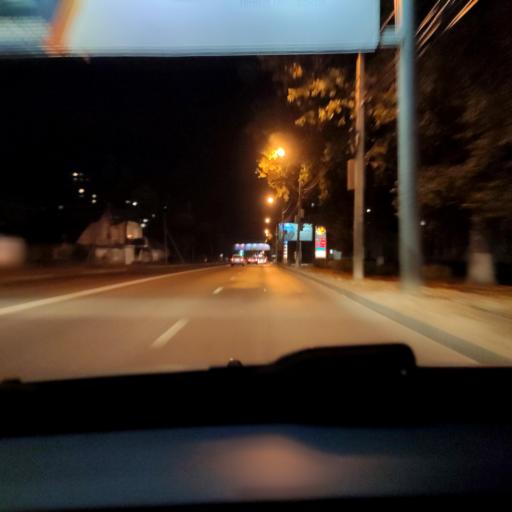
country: RU
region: Voronezj
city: Voronezh
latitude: 51.6968
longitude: 39.1967
